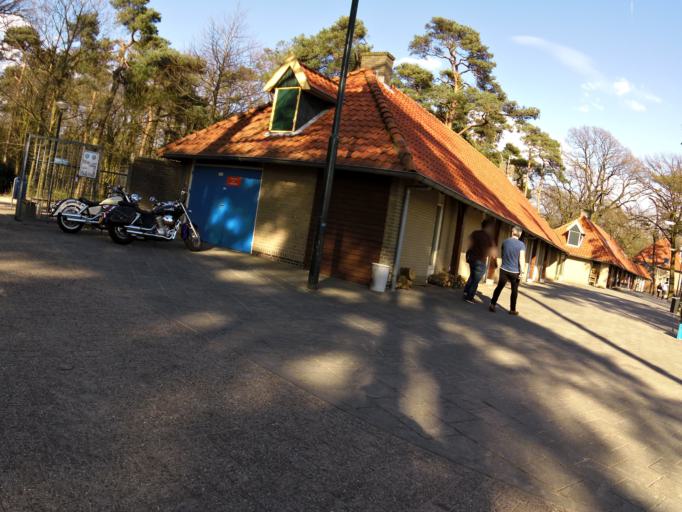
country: NL
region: North Brabant
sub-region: Gemeente Vught
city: Vught
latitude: 51.6544
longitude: 5.2572
